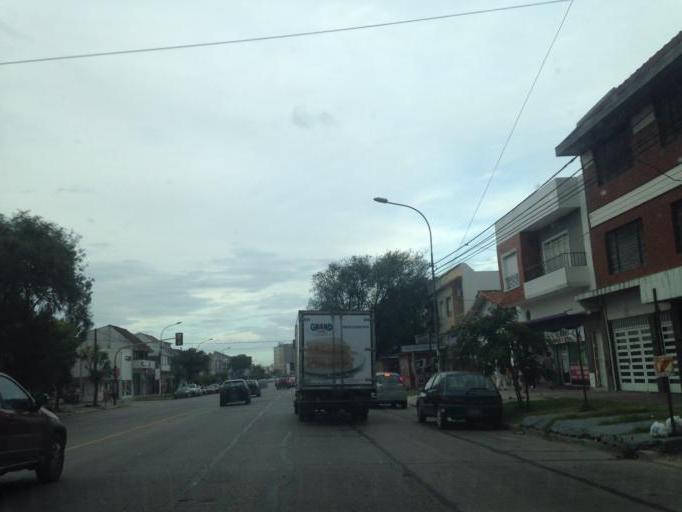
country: AR
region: Buenos Aires
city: Mar del Plata
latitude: -38.0236
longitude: -57.5767
